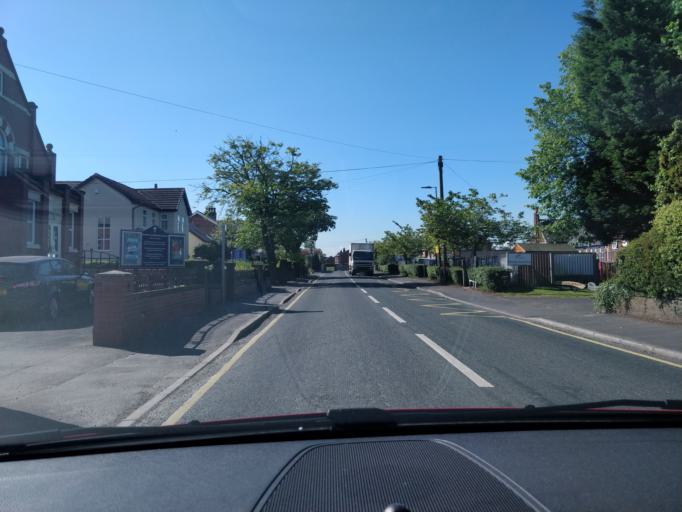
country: GB
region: England
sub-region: Lancashire
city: Tarleton
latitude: 53.6920
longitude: -2.8357
